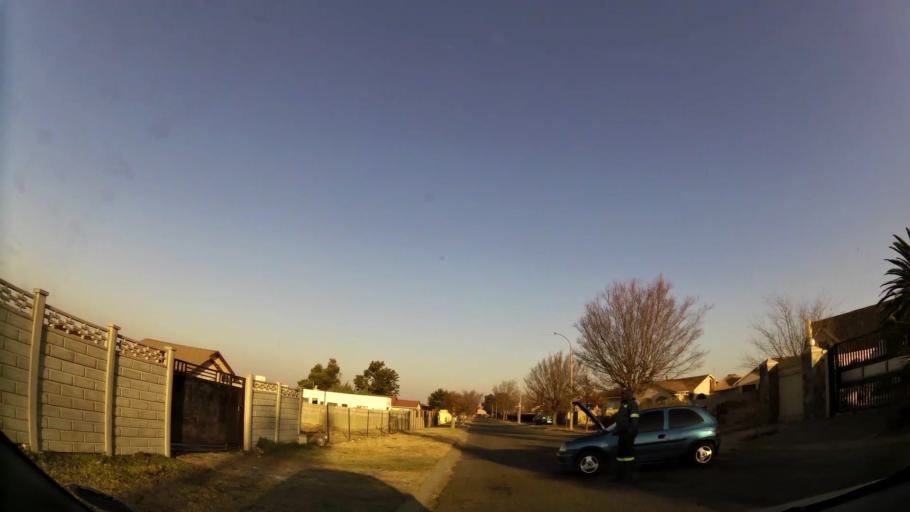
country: ZA
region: Gauteng
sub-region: West Rand District Municipality
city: Randfontein
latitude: -26.2030
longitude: 27.6568
